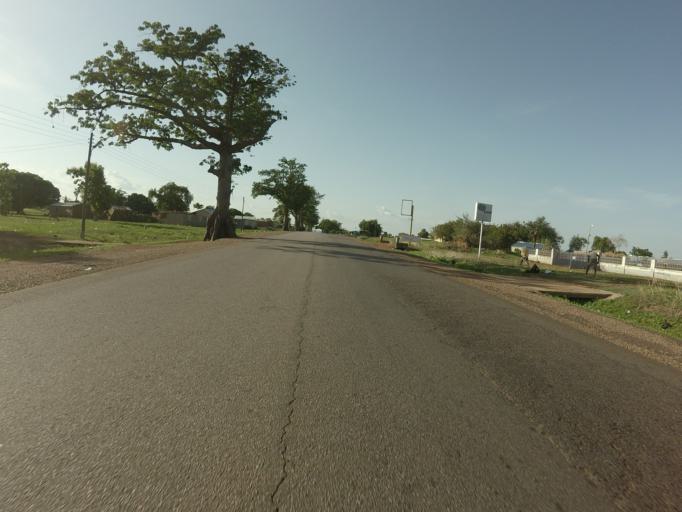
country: GH
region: Upper East
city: Navrongo
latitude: 10.9183
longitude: -1.0896
